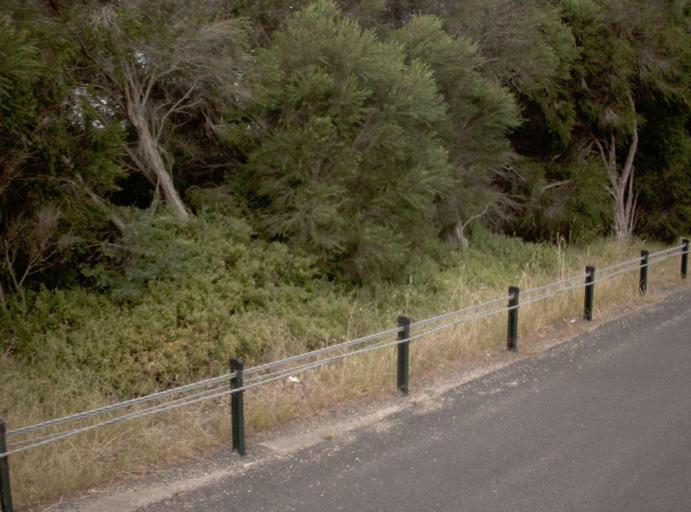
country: AU
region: Victoria
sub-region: East Gippsland
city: Bairnsdale
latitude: -37.8673
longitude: 147.6485
